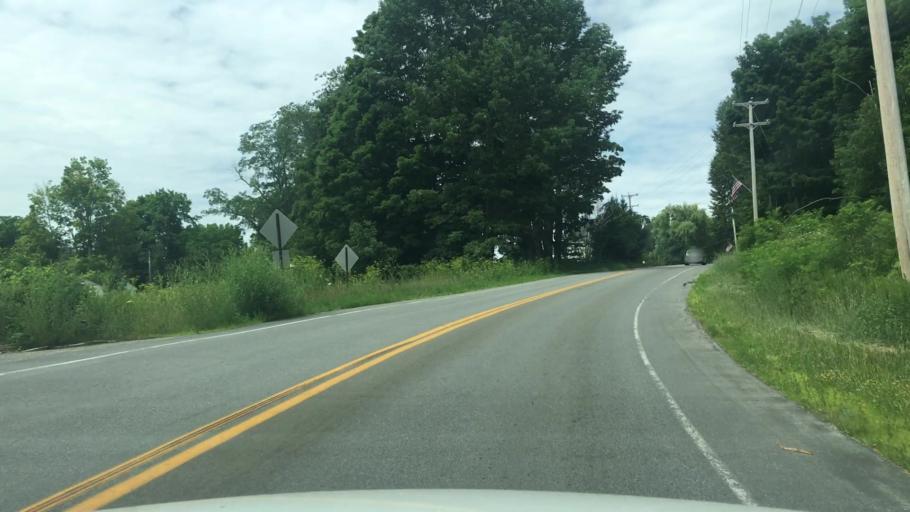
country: US
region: Maine
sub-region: Waldo County
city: Troy
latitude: 44.5300
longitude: -69.2964
